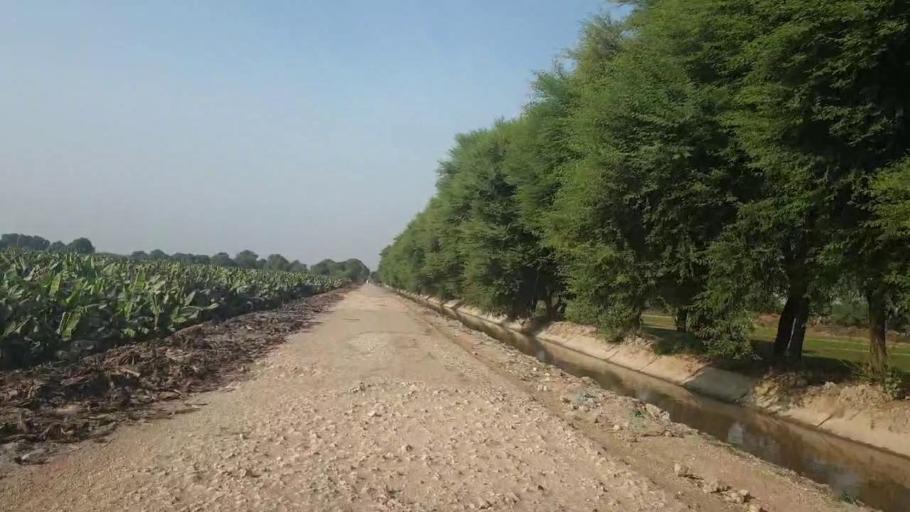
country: PK
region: Sindh
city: Tando Jam
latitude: 25.4170
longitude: 68.4639
